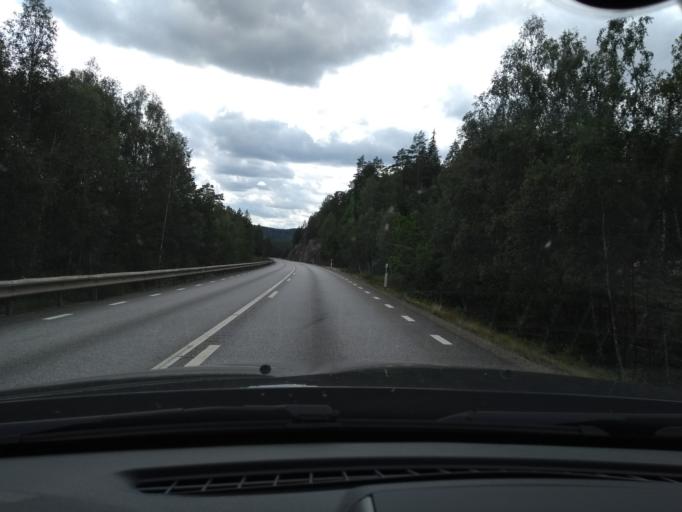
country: SE
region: Kalmar
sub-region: Vimmerby Kommun
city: Vimmerby
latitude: 57.6407
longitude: 15.7659
